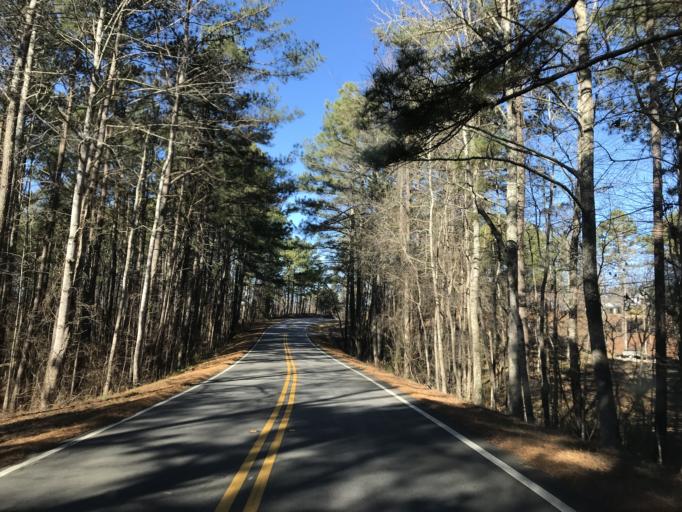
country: US
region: Georgia
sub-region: Paulding County
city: Dallas
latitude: 33.9825
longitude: -84.8843
